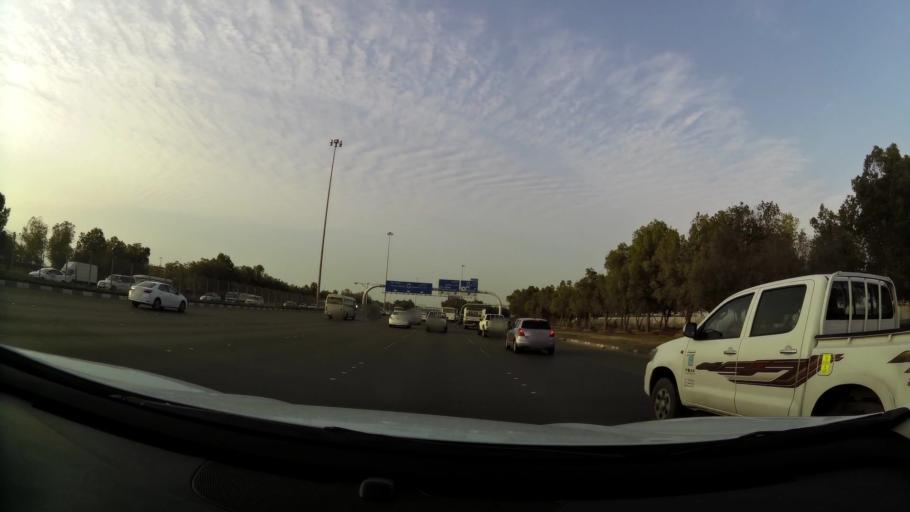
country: AE
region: Abu Dhabi
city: Abu Dhabi
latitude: 24.3858
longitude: 54.5245
